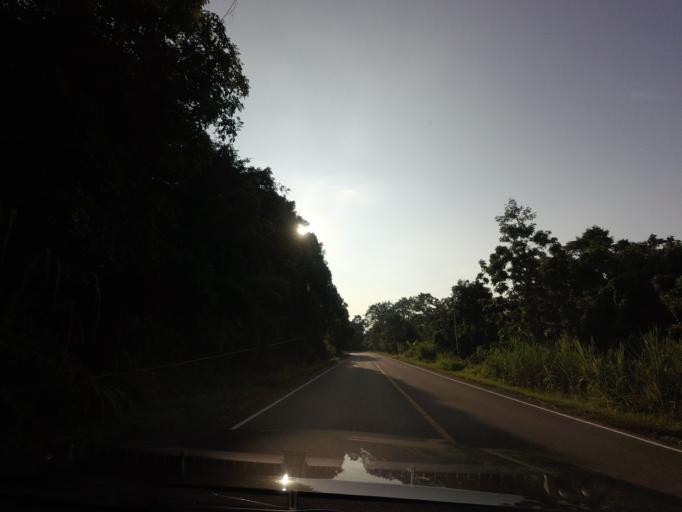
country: TH
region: Nan
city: Na Noi
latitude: 18.3627
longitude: 100.8245
